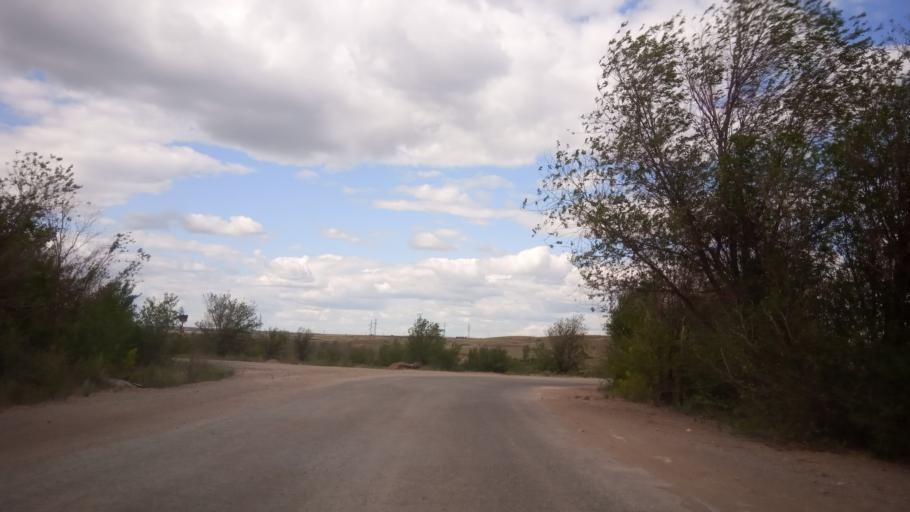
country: RU
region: Orenburg
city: Novotroitsk
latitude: 51.2527
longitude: 58.3666
